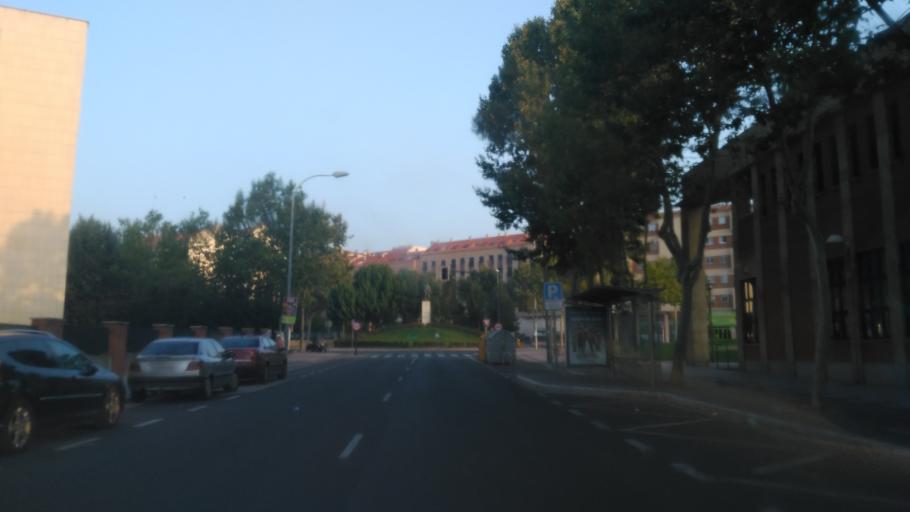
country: ES
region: Castille and Leon
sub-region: Provincia de Salamanca
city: Salamanca
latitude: 40.9722
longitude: -5.6765
